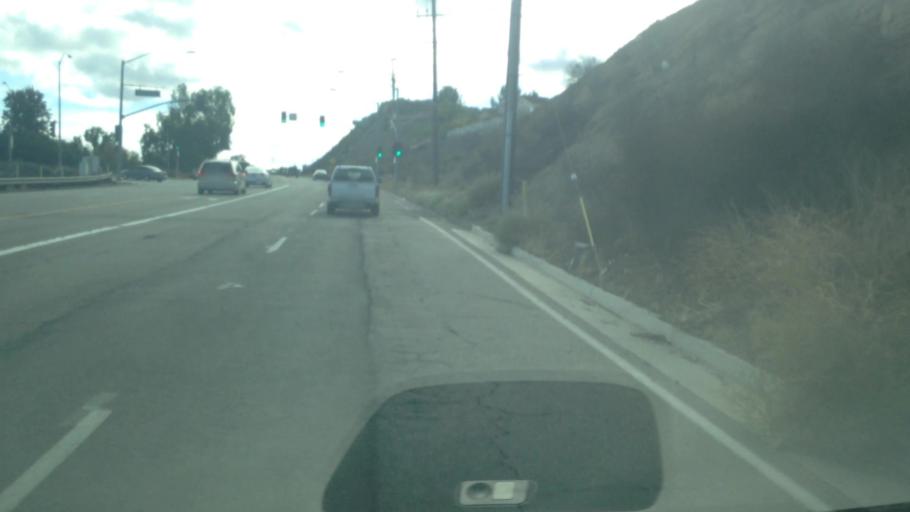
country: US
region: California
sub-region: Riverside County
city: Home Gardens
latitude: 33.8634
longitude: -117.4539
